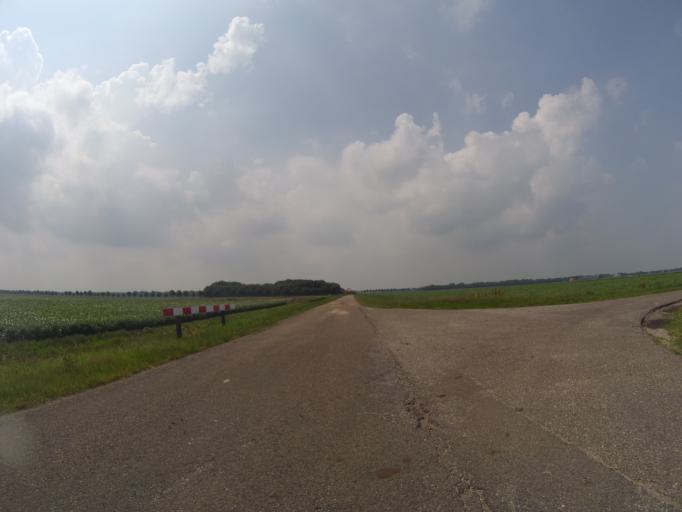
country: NL
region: Drenthe
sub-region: Gemeente Emmen
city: Emmer-Compascuum
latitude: 52.7850
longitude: 7.0042
